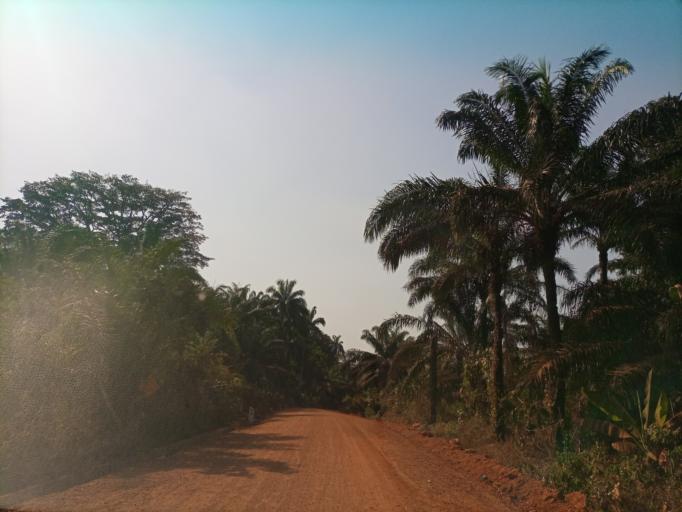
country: NG
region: Enugu
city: Aku
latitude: 6.7007
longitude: 7.3201
